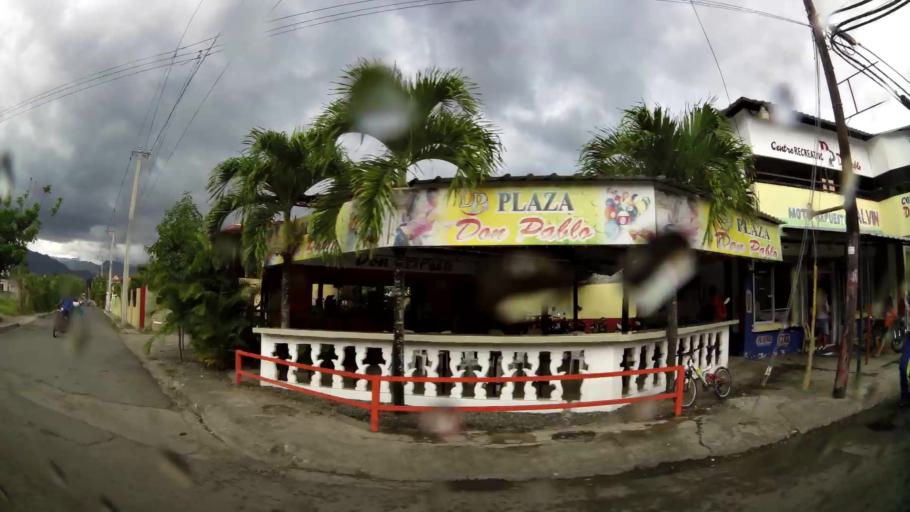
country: DO
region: Monsenor Nouel
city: Bonao
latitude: 18.9305
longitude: -70.4026
